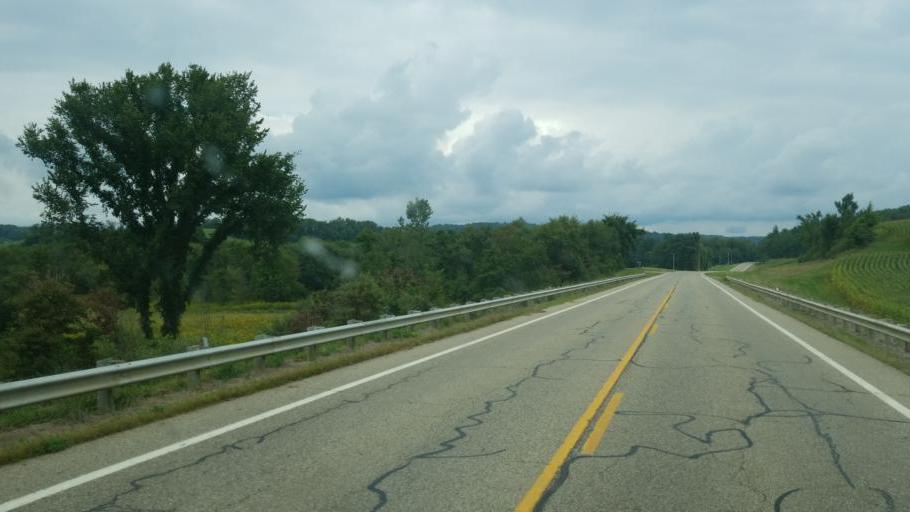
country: US
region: Ohio
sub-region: Knox County
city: Danville
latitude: 40.5437
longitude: -82.2983
